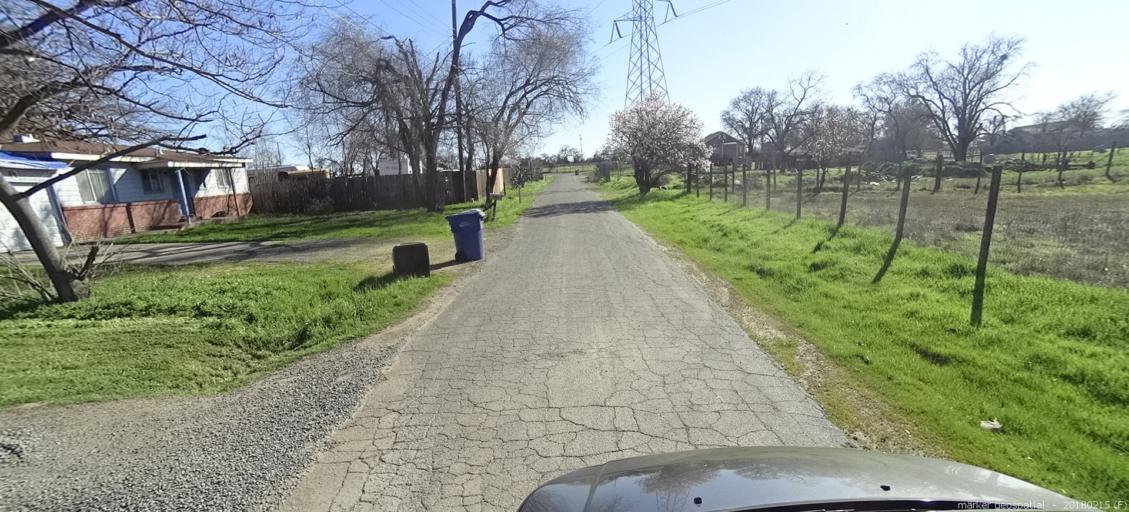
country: US
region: California
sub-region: Sacramento County
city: Rio Linda
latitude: 38.6707
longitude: -121.4615
